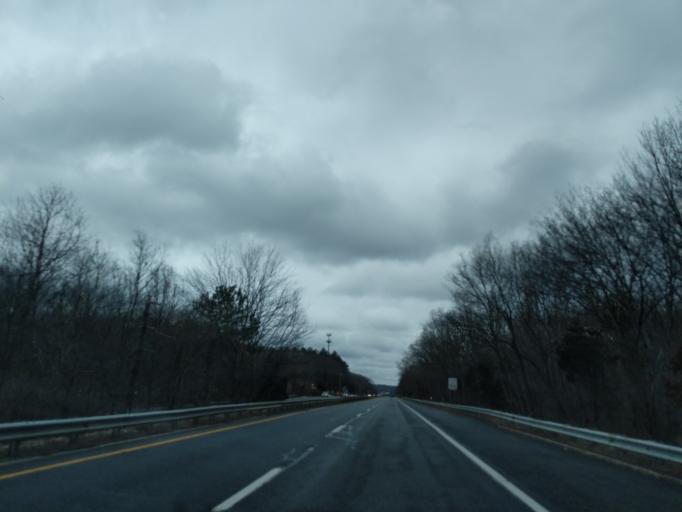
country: US
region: Rhode Island
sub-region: Providence County
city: Woonsocket
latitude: 41.9706
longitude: -71.5099
